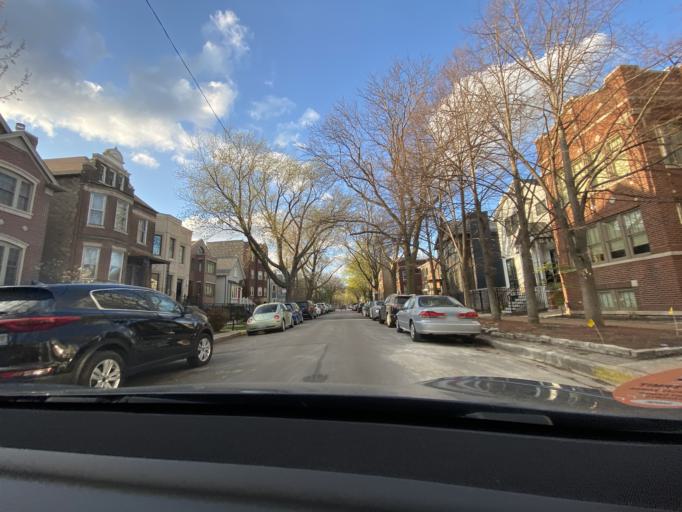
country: US
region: Illinois
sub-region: Cook County
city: Lincolnwood
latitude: 41.9478
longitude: -87.6701
